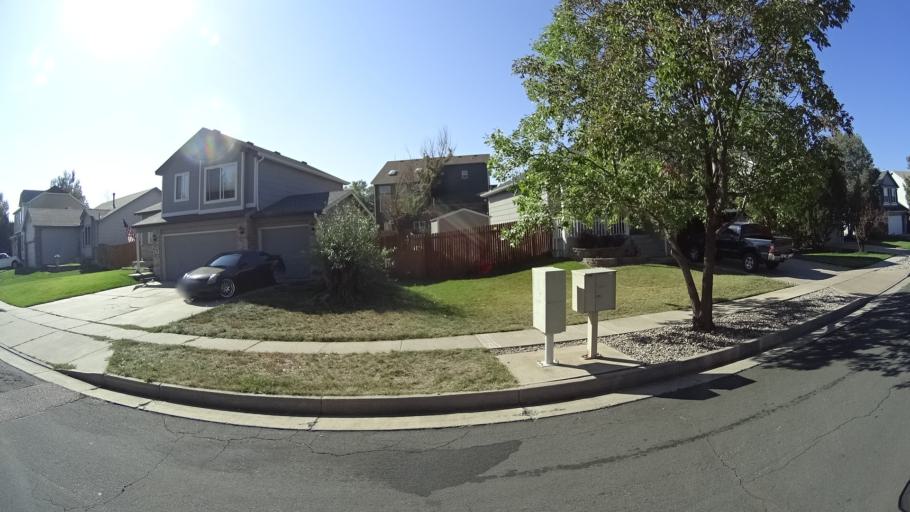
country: US
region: Colorado
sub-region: El Paso County
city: Cimarron Hills
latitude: 38.8844
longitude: -104.7054
